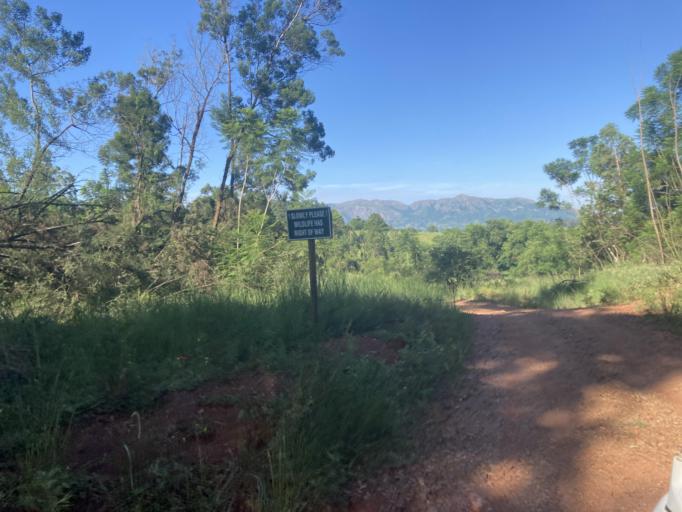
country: SZ
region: Hhohho
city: Lobamba
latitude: -26.4914
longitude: 31.1873
